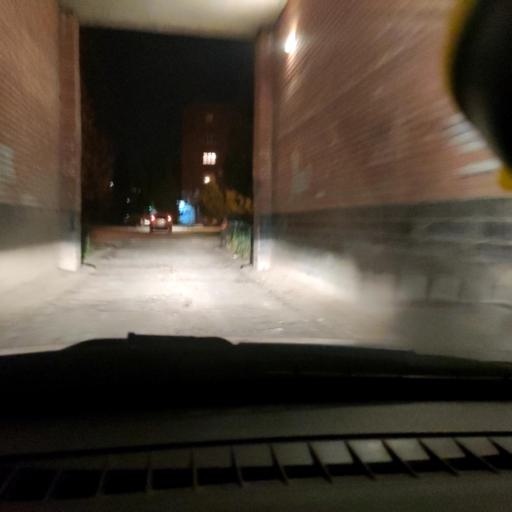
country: RU
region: Samara
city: Tol'yatti
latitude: 53.5339
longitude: 49.2682
